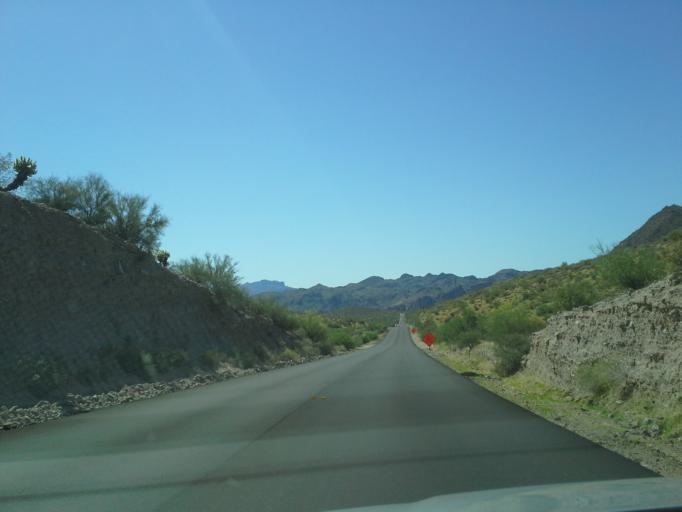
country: US
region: Arizona
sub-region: Maricopa County
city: Fountain Hills
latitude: 33.6081
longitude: -111.5485
